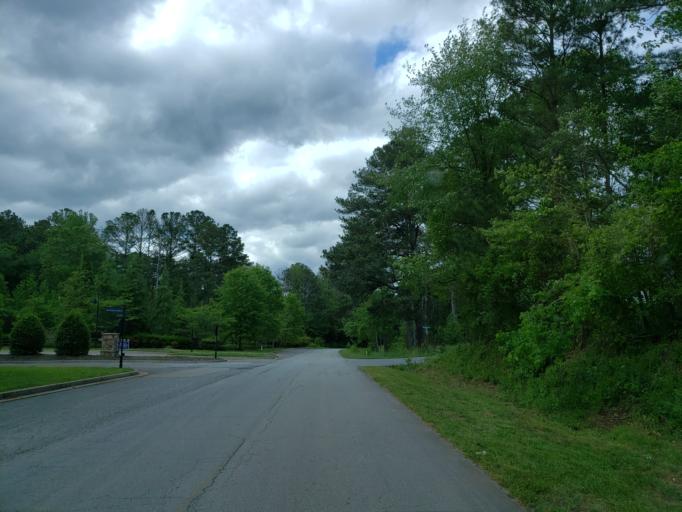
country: US
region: Georgia
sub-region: Haralson County
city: Tallapoosa
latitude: 33.7238
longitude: -85.2931
